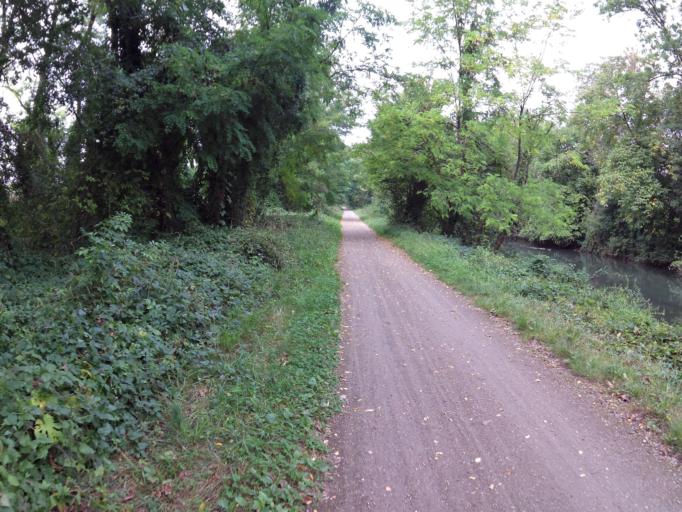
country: FR
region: Alsace
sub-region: Departement du Haut-Rhin
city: Kunheim
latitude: 48.1185
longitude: 7.5330
